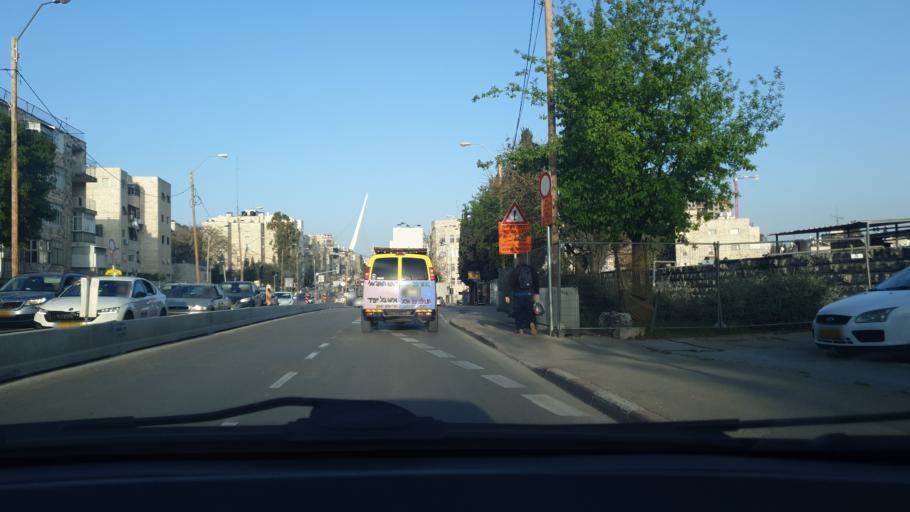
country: IL
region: Jerusalem
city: West Jerusalem
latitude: 31.7875
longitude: 35.1914
